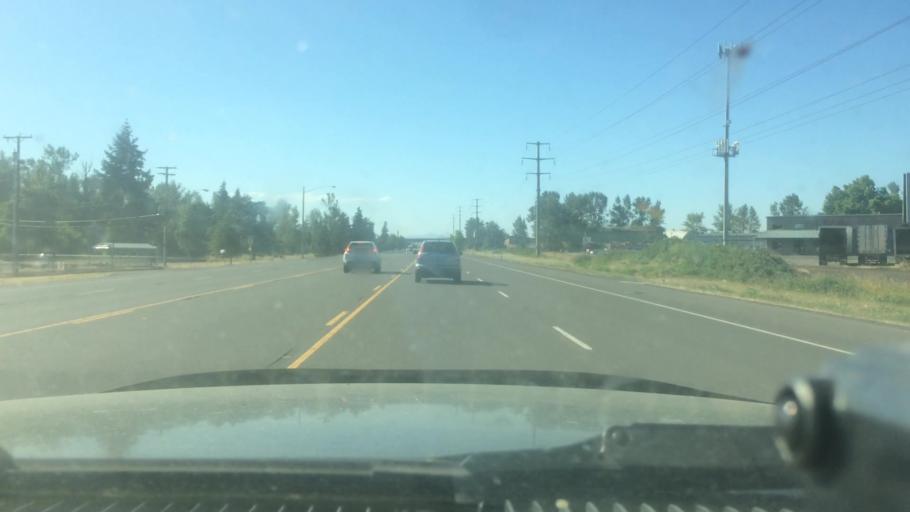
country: US
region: Oregon
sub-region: Lane County
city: Eugene
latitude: 44.0910
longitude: -123.1606
